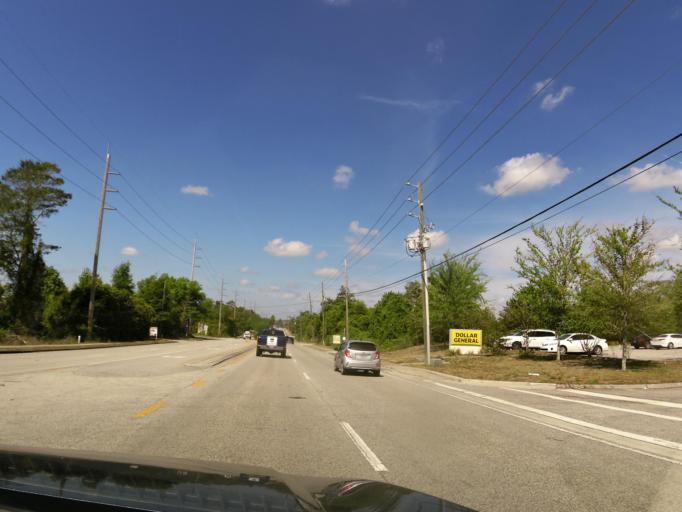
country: US
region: Florida
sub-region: Volusia County
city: Lake Helen
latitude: 28.9479
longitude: -81.2343
